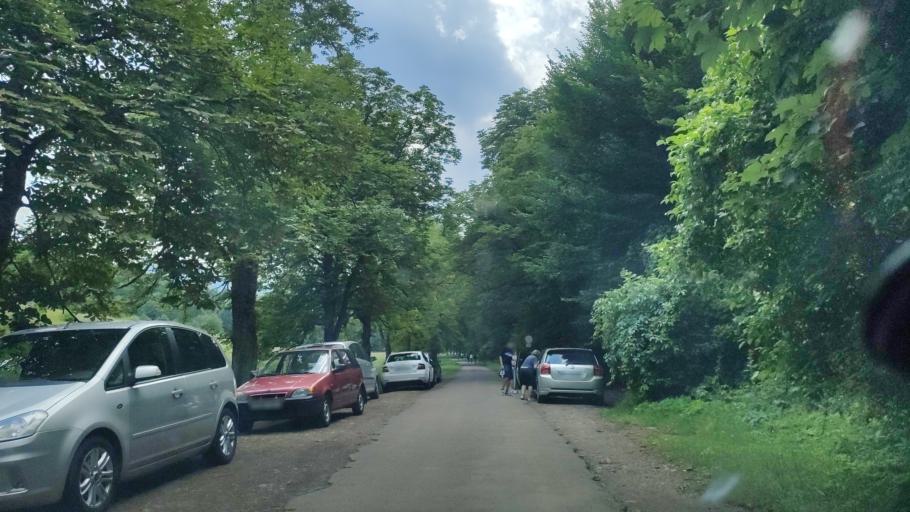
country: HU
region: Heves
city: Parad
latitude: 47.8986
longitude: 20.0565
